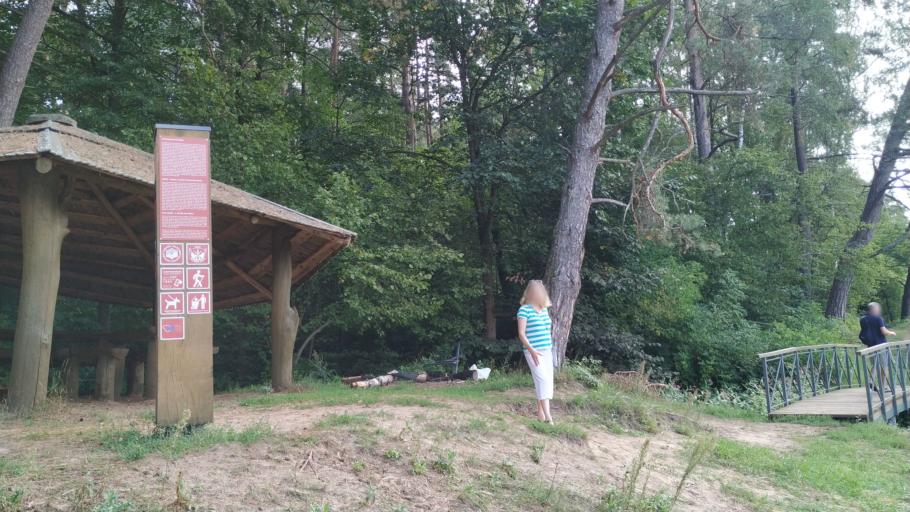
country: LT
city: Grigiskes
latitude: 54.8073
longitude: 24.9663
